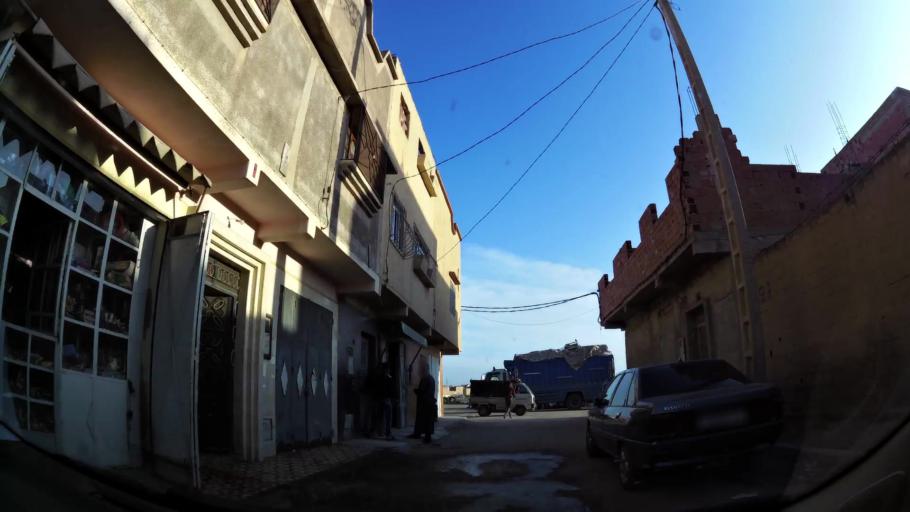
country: MA
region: Oriental
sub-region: Oujda-Angad
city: Oujda
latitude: 34.7066
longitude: -1.9076
